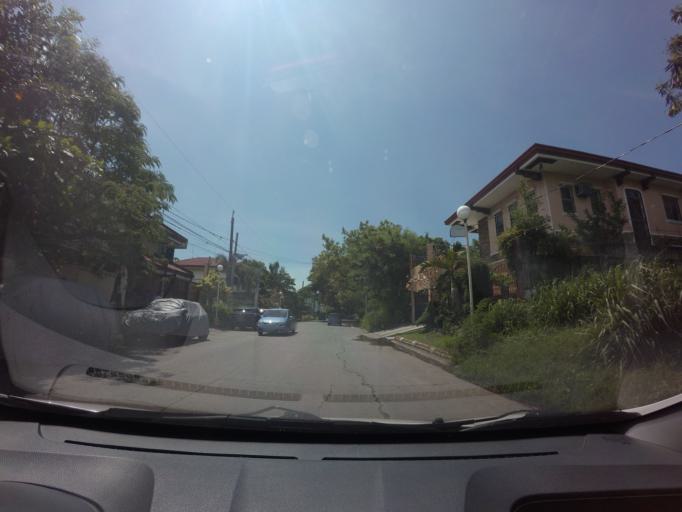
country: PH
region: Calabarzon
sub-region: Province of Rizal
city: Las Pinas
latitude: 14.4291
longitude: 120.9861
